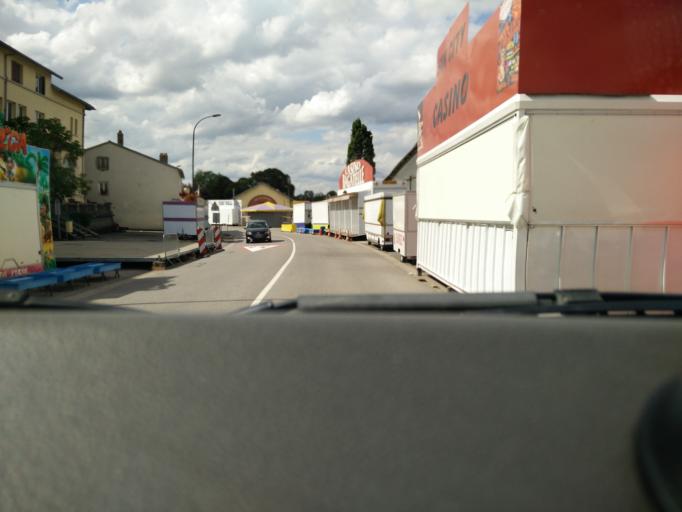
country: FR
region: Lorraine
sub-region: Departement de Meurthe-et-Moselle
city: Damelevieres
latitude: 48.5576
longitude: 6.3858
